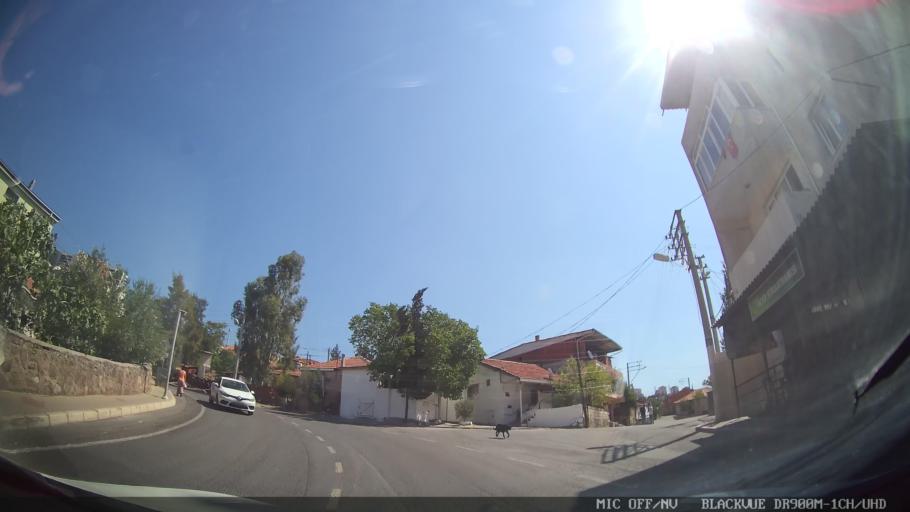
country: TR
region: Izmir
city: Karsiyaka
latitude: 38.5026
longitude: 27.0785
